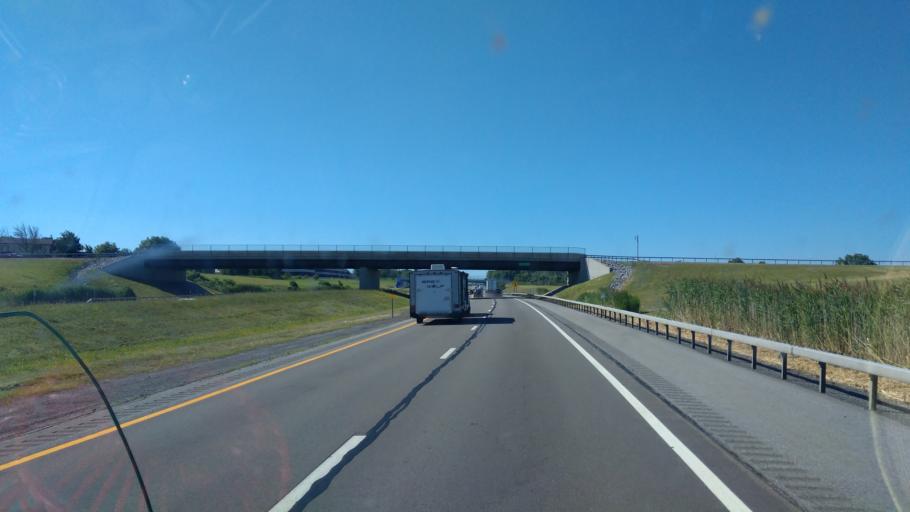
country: US
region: New York
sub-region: Erie County
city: Blasdell
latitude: 42.7948
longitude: -78.8170
